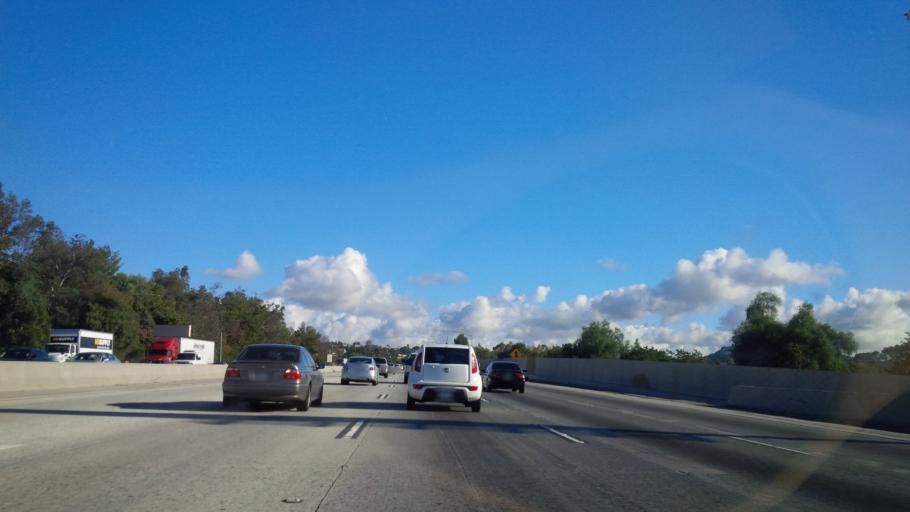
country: US
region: California
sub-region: Los Angeles County
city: Walnut
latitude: 33.9704
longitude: -117.8473
